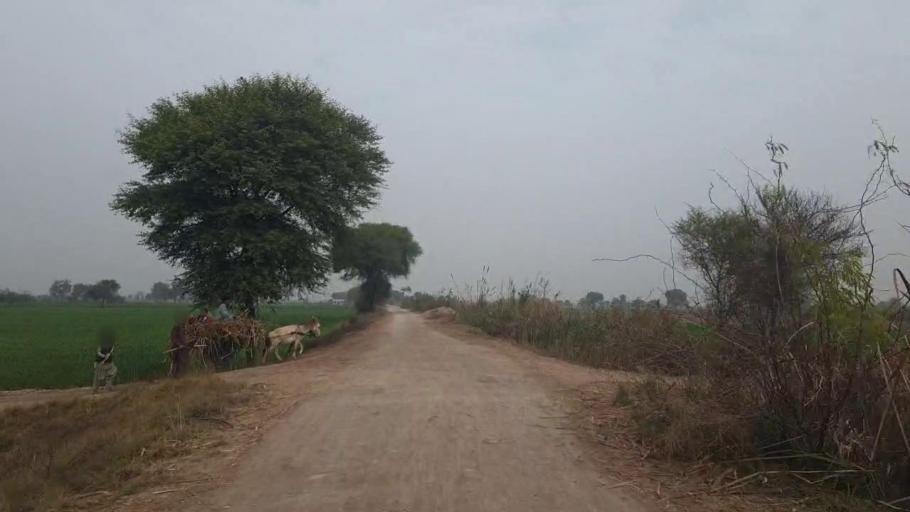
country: PK
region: Sindh
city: Tando Adam
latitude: 25.7255
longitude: 68.7386
